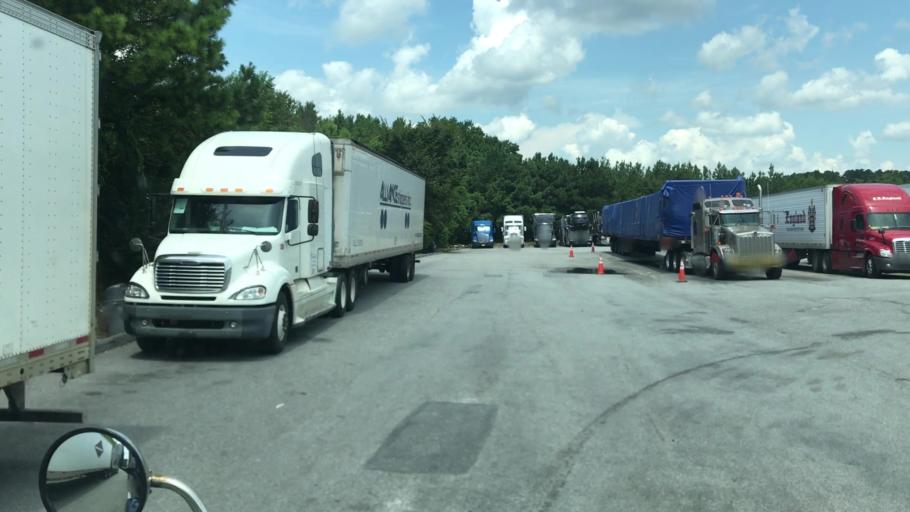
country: US
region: Georgia
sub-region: Bartow County
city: Cartersville
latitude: 34.2749
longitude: -84.8092
